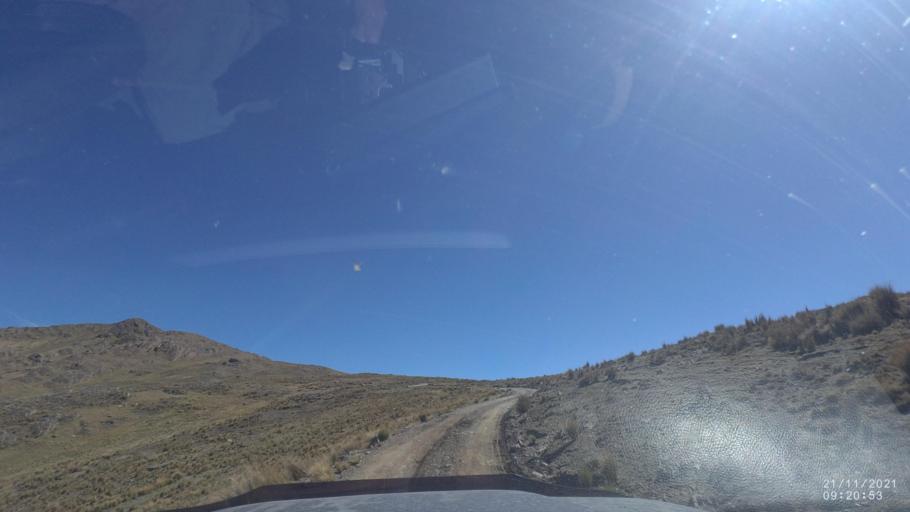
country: BO
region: Cochabamba
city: Cochabamba
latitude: -17.1079
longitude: -66.2507
